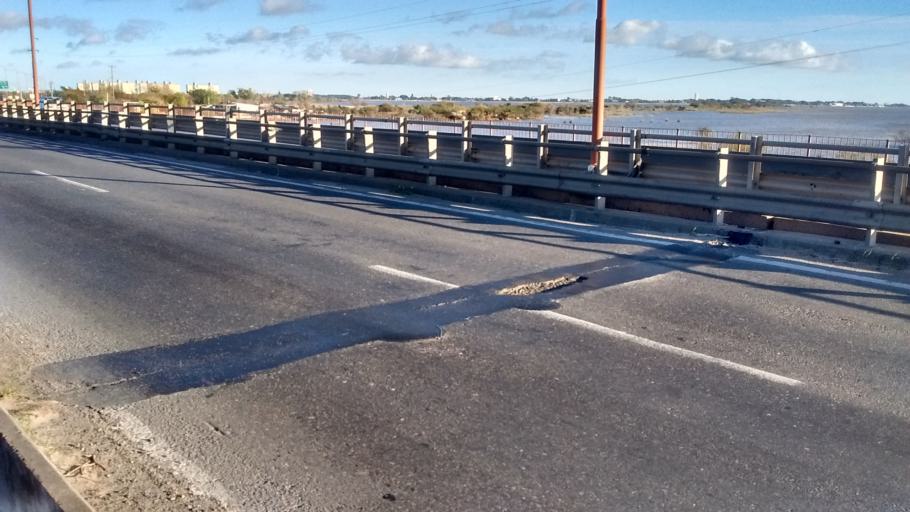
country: AR
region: Santa Fe
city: Santa Fe de la Vera Cruz
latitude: -31.6402
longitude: -60.6406
